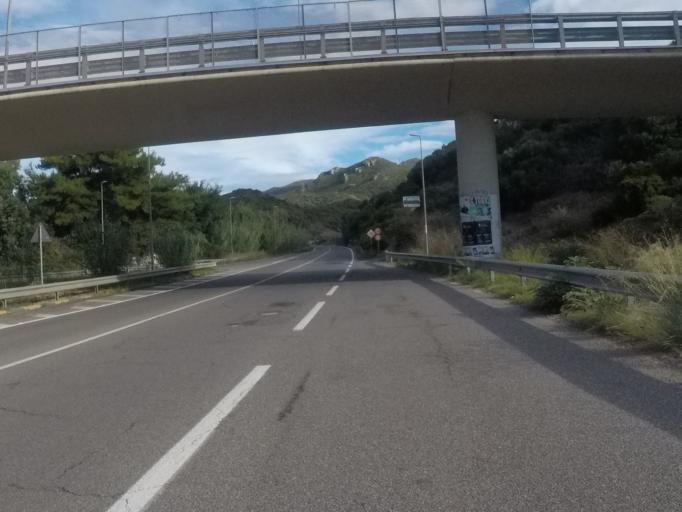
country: IT
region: Sardinia
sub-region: Provincia di Carbonia-Iglesias
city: Gonnesa
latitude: 39.2773
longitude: 8.4683
